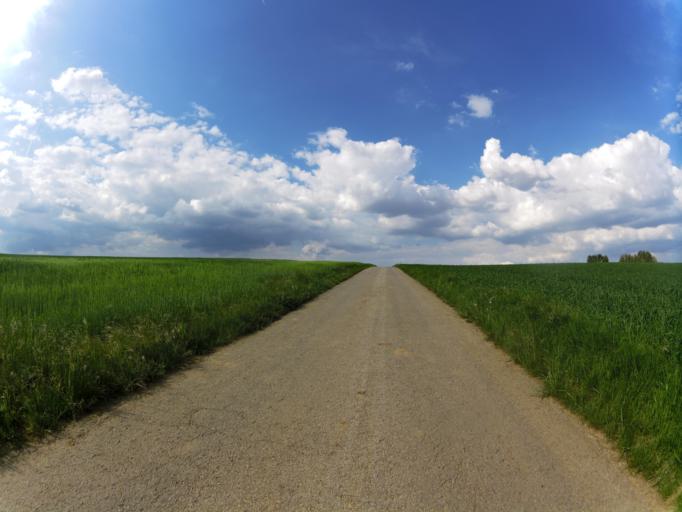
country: DE
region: Bavaria
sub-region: Regierungsbezirk Unterfranken
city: Giebelstadt
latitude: 49.6248
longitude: 9.9381
